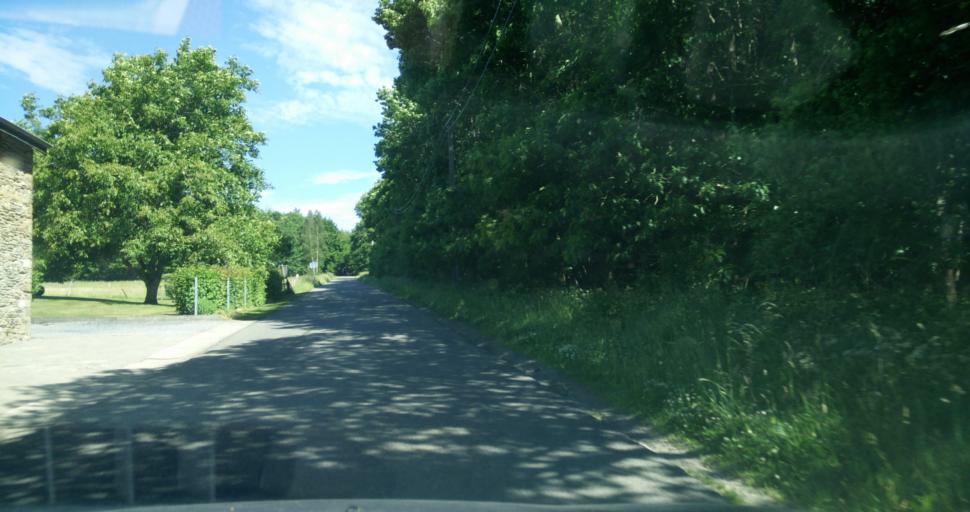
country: BE
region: Wallonia
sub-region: Province du Luxembourg
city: La Roche-en-Ardenne
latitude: 50.1869
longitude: 5.6735
